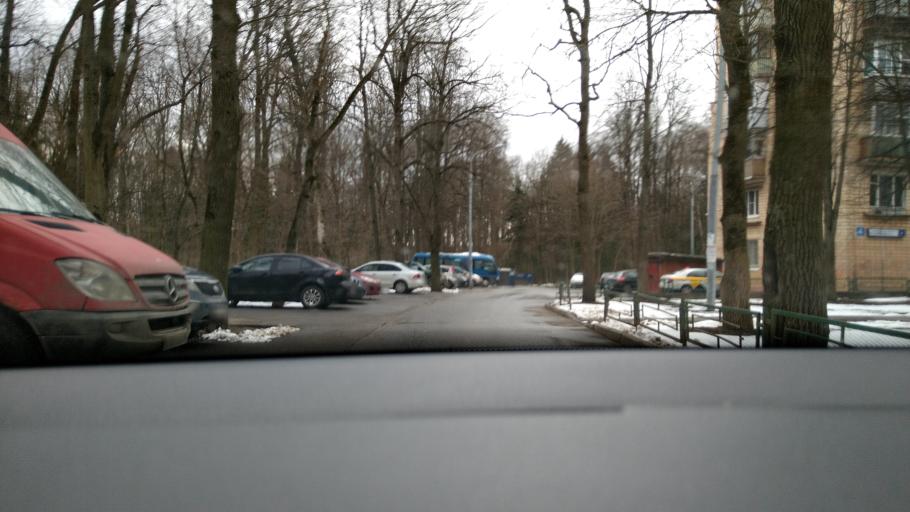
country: RU
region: Moskovskaya
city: Moskovskiy
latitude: 55.6003
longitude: 37.3346
